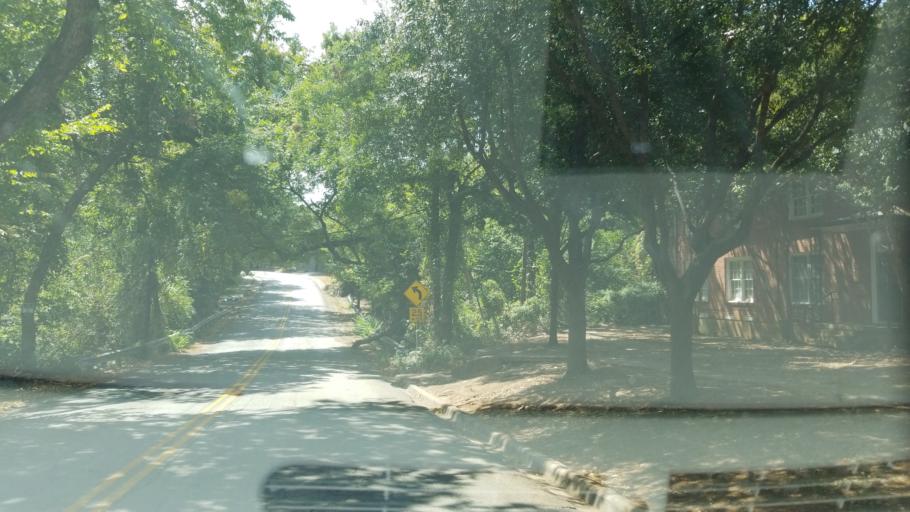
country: US
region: Texas
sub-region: Dallas County
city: Cockrell Hill
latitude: 32.7628
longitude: -96.8507
